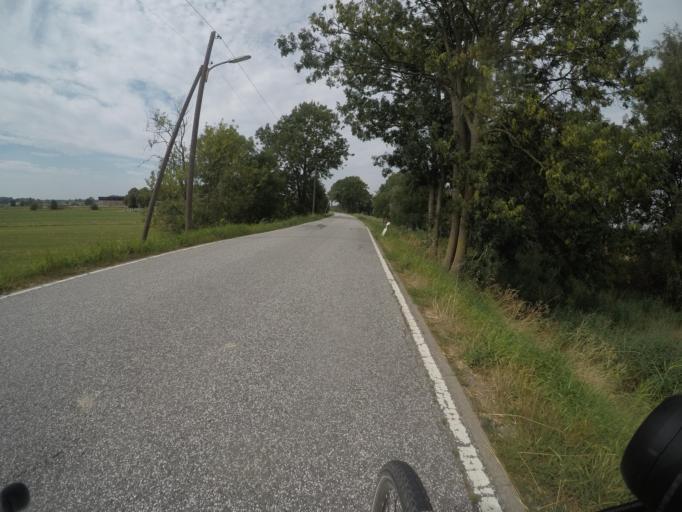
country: DE
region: Schleswig-Holstein
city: Oststeinbek
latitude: 53.4730
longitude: 10.1371
